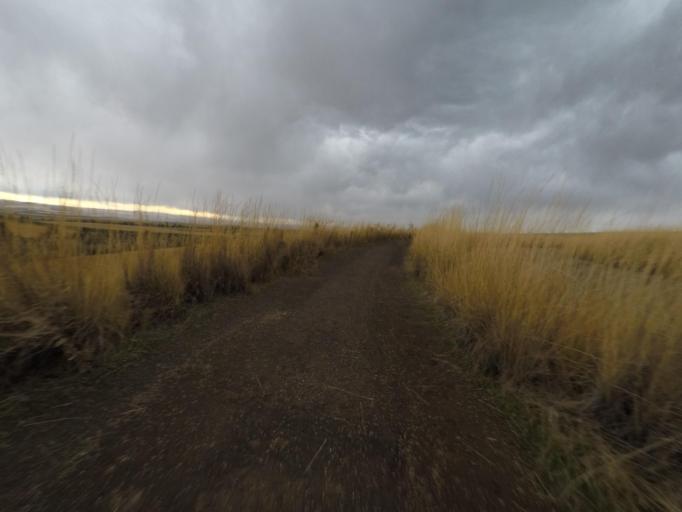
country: US
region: Washington
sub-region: Walla Walla County
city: Walla Walla East
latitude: 46.0629
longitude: -118.2668
